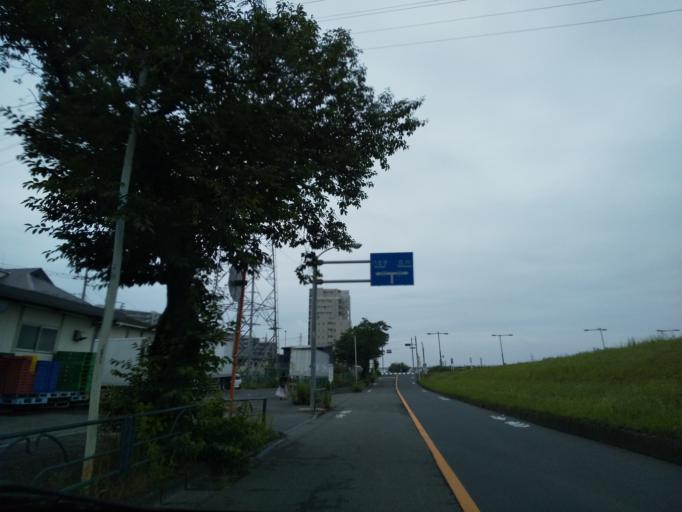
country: JP
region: Tokyo
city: Hino
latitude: 35.6808
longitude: 139.4125
